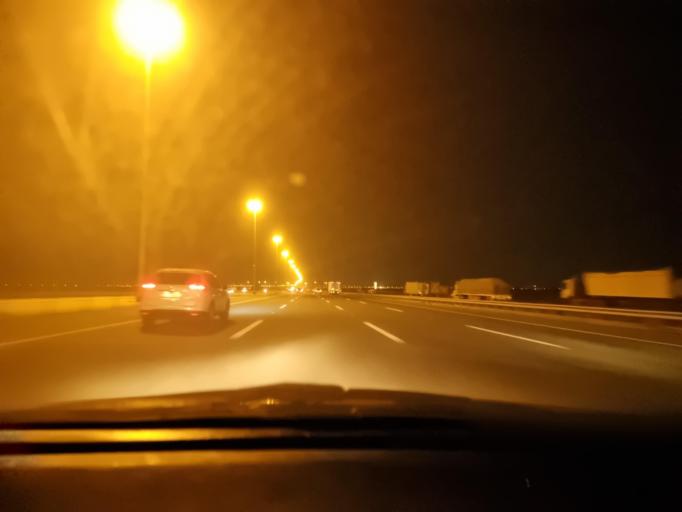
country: AE
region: Abu Dhabi
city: Abu Dhabi
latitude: 24.6392
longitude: 54.7837
